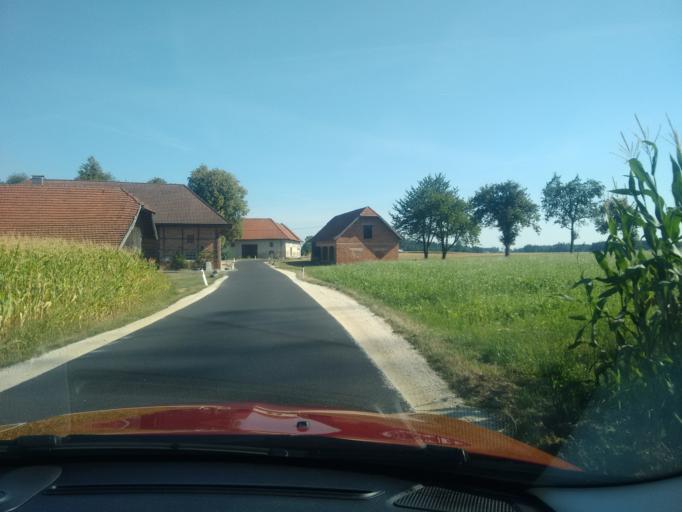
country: AT
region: Upper Austria
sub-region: Wels-Land
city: Sattledt
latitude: 48.0860
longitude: 14.0748
